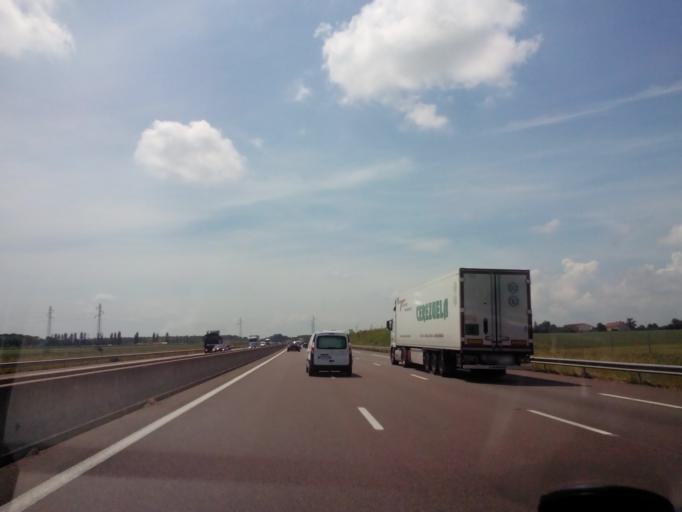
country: FR
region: Bourgogne
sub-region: Departement de la Cote-d'Or
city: Nuits-Saint-Georges
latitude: 47.0896
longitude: 4.9370
